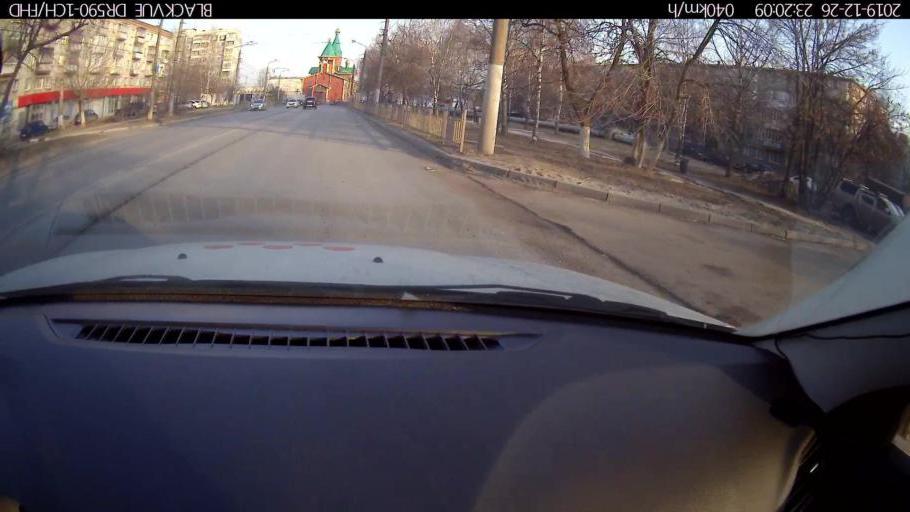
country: RU
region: Nizjnij Novgorod
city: Burevestnik
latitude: 56.2319
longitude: 43.8766
